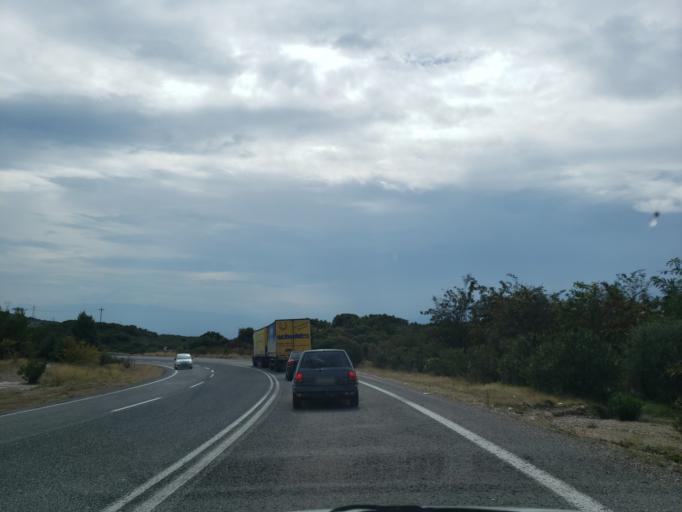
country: GR
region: Central Greece
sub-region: Nomos Fthiotidos
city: Stavros
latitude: 38.9713
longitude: 22.3842
